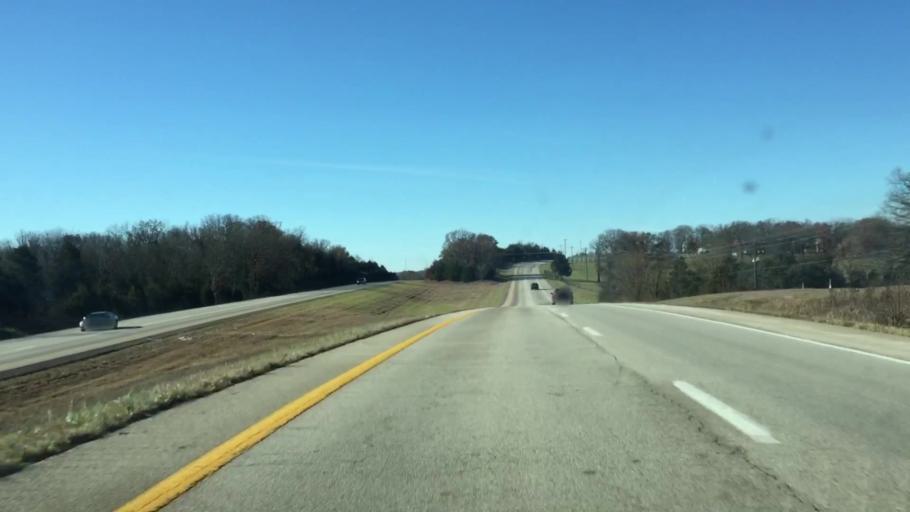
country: US
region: Missouri
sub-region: Cole County
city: Wardsville
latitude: 38.4348
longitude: -92.3114
